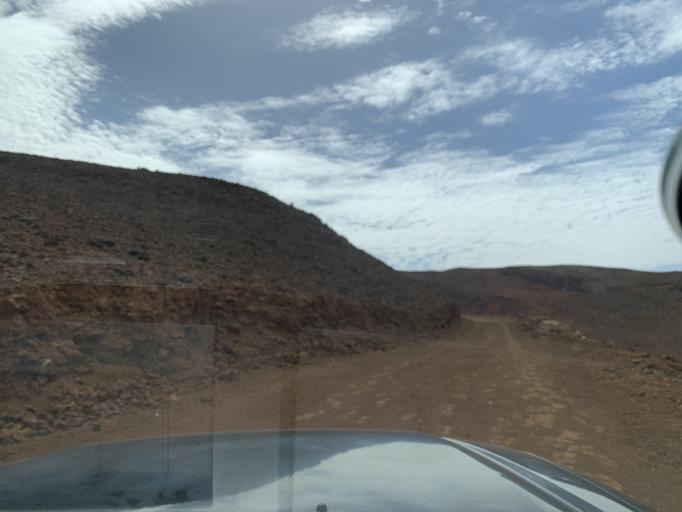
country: CV
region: Porto Novo
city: Porto Novo
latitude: 16.9653
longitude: -25.2707
